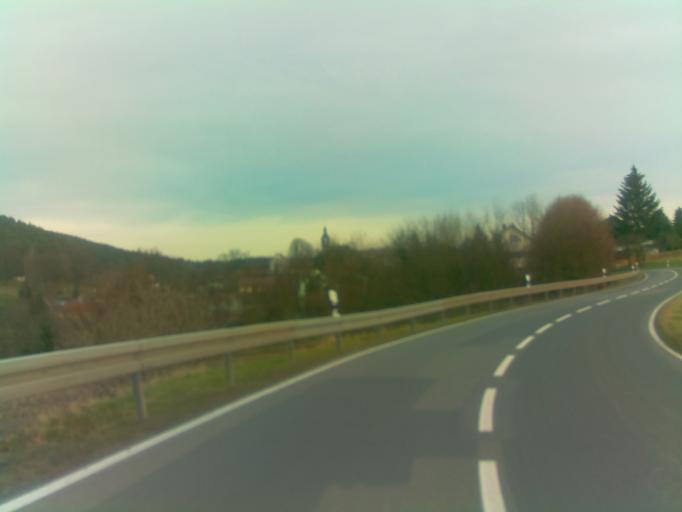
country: DE
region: Thuringia
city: Ruttersdorf-Lotschen
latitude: 50.8833
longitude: 11.7400
